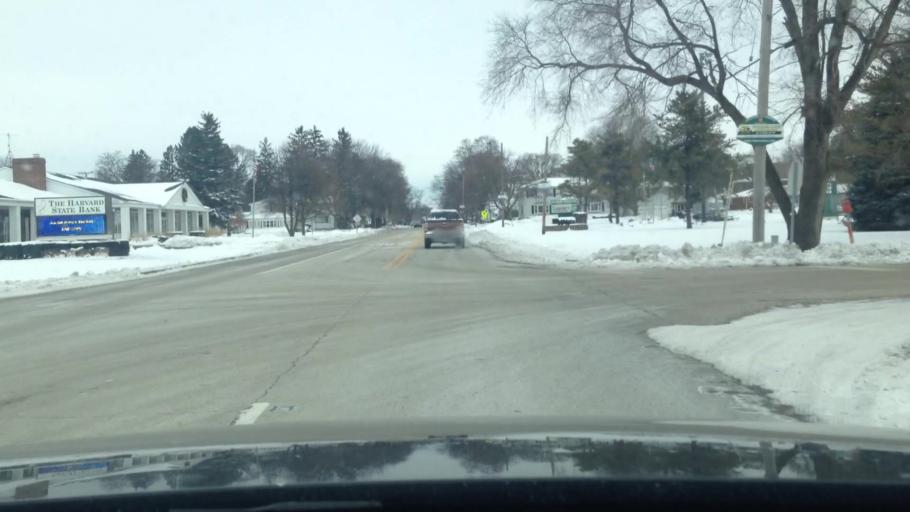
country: US
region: Illinois
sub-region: McHenry County
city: Hebron
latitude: 42.4648
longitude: -88.4328
